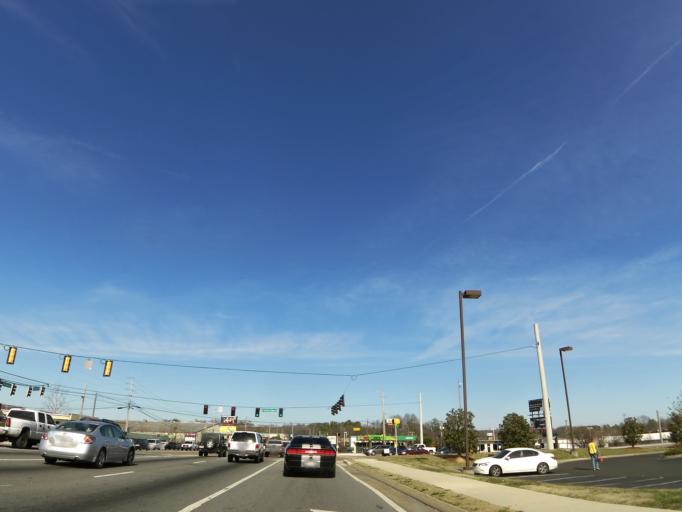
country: US
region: Georgia
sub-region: Whitfield County
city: Dalton
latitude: 34.7973
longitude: -84.9620
